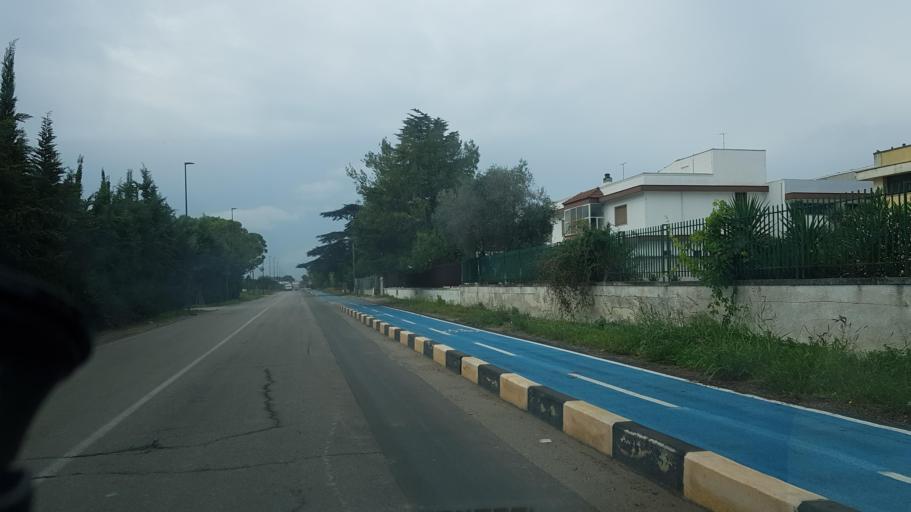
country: IT
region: Apulia
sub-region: Provincia di Lecce
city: Guagnano
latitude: 40.4116
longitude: 17.9585
